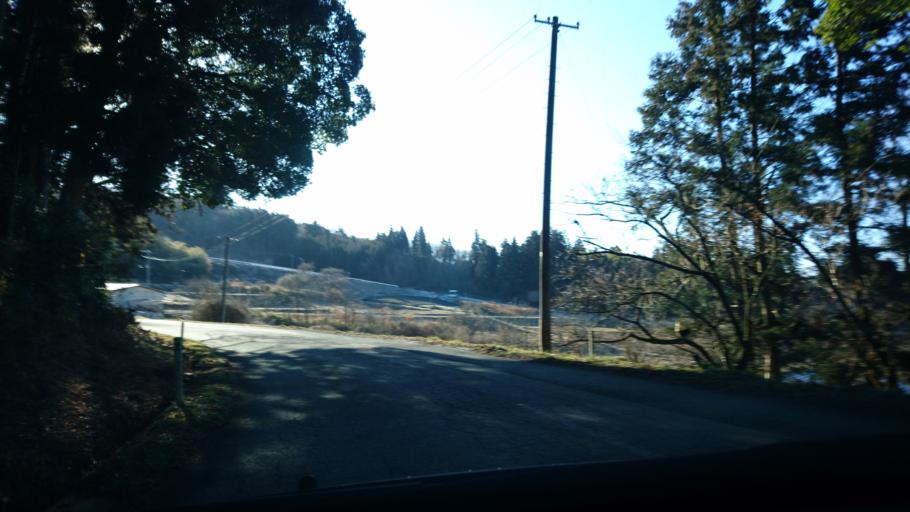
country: JP
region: Iwate
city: Ichinoseki
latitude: 38.8710
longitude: 141.2947
